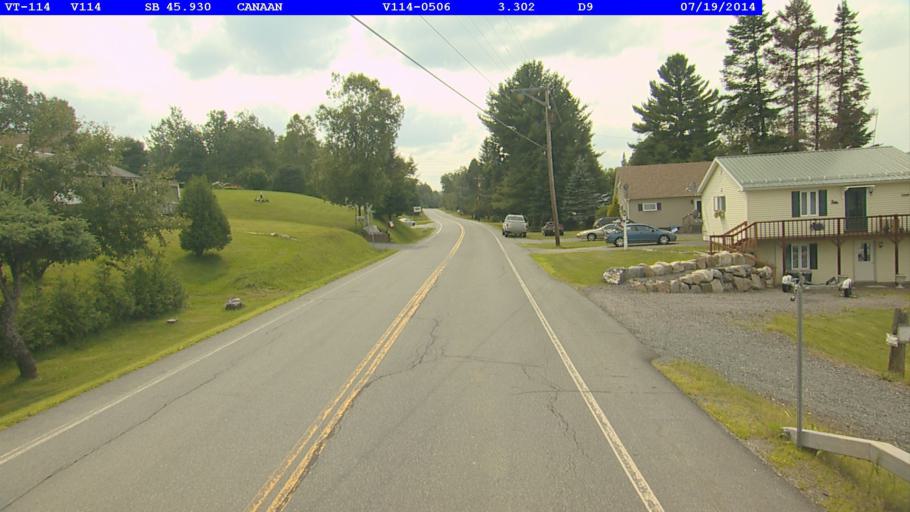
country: US
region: New Hampshire
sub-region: Coos County
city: Colebrook
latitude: 45.0099
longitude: -71.6279
